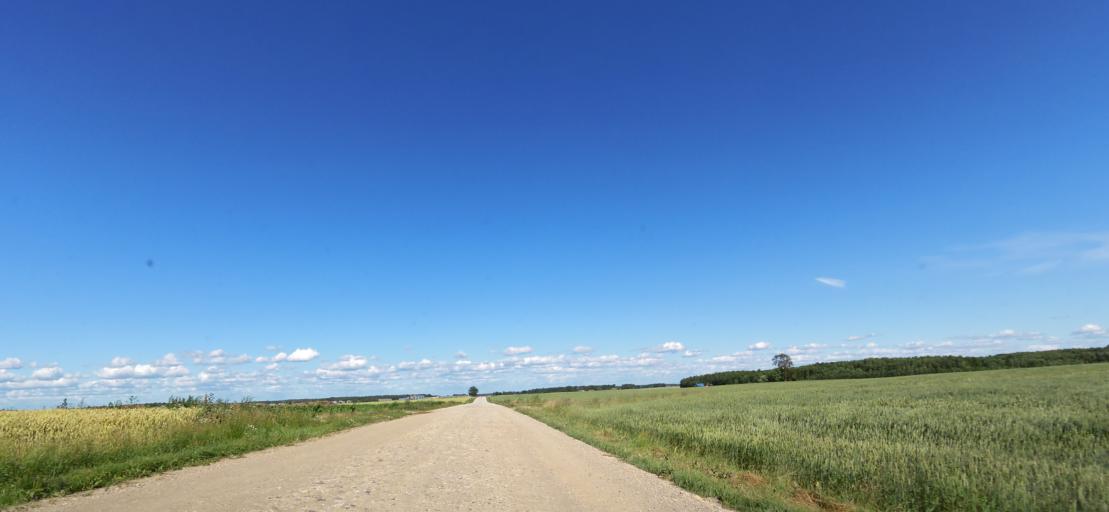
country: LT
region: Panevezys
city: Pasvalys
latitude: 56.1233
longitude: 24.3658
